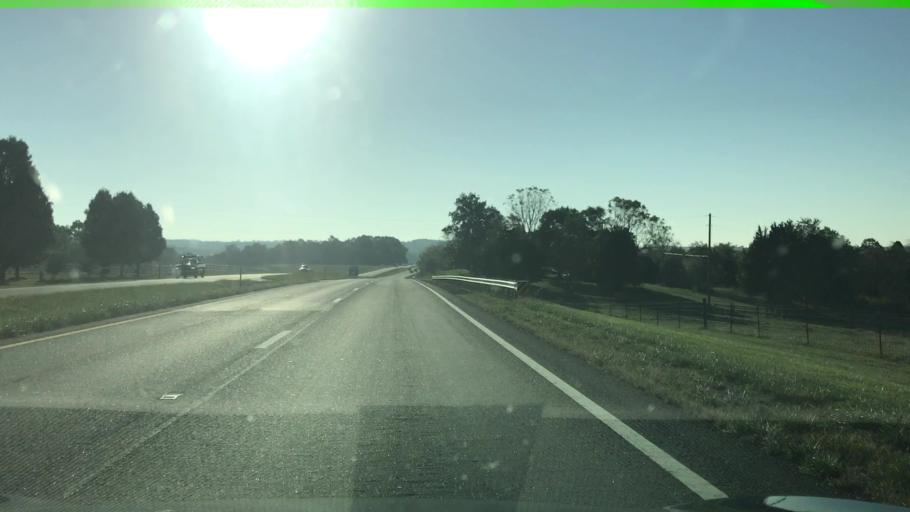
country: US
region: Virginia
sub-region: City of Bedford
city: Bedford
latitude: 37.3159
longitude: -79.4125
